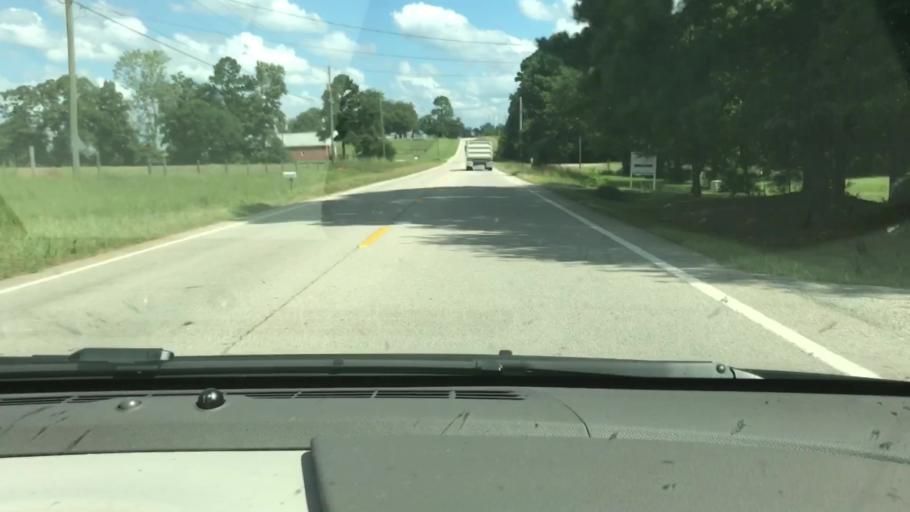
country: US
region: Georgia
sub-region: Troup County
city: West Point
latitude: 32.8739
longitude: -85.0345
